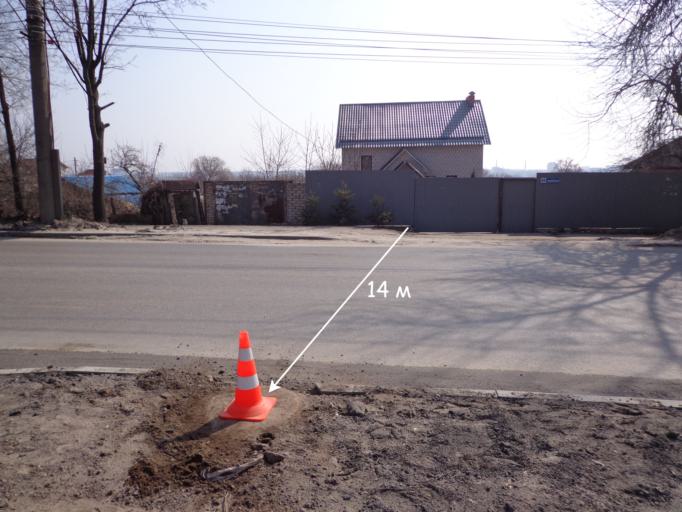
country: RU
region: Voronezj
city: Voronezh
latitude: 51.7010
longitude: 39.2330
